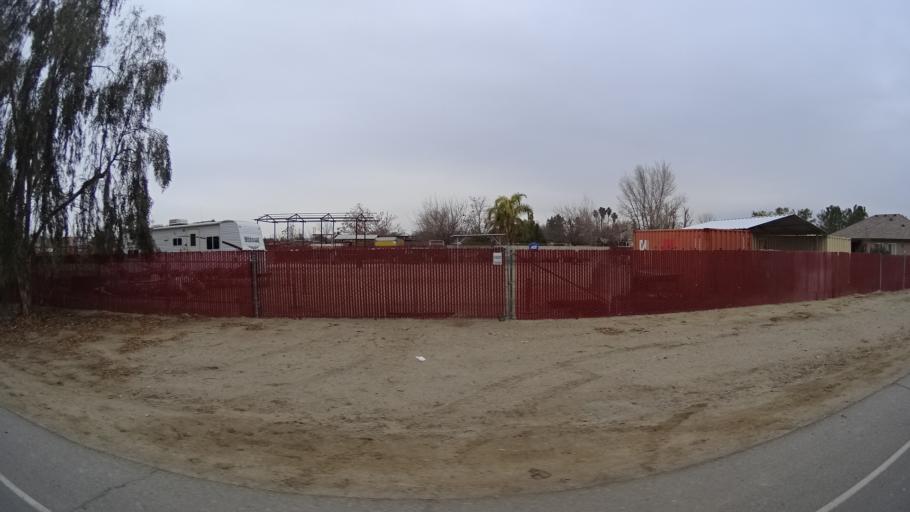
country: US
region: California
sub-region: Kern County
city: Bakersfield
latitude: 35.3470
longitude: -118.9397
